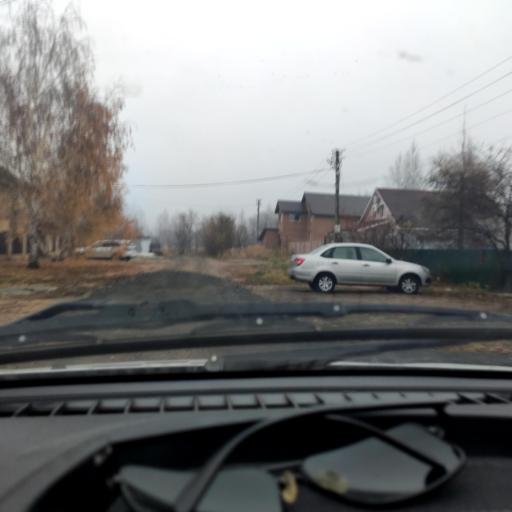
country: RU
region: Samara
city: Tol'yatti
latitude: 53.5521
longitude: 49.3805
